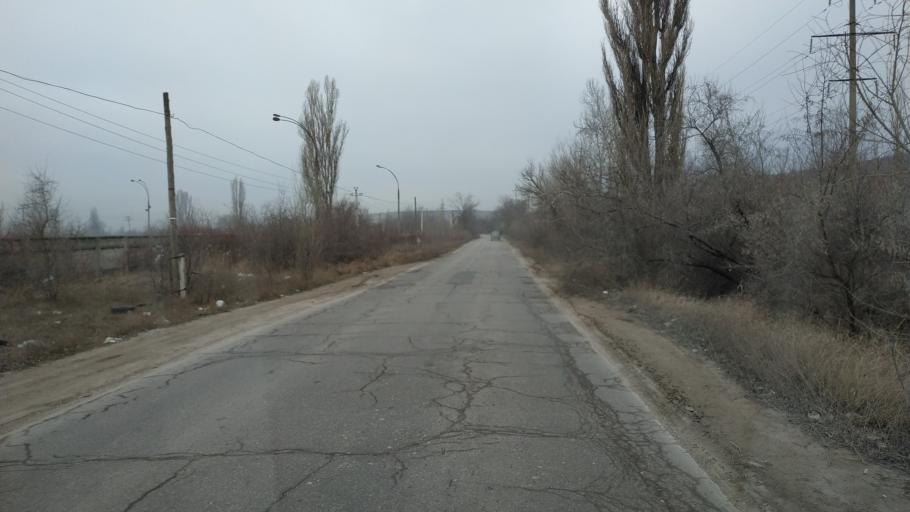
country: MD
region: Chisinau
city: Vatra
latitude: 47.0696
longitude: 28.7759
